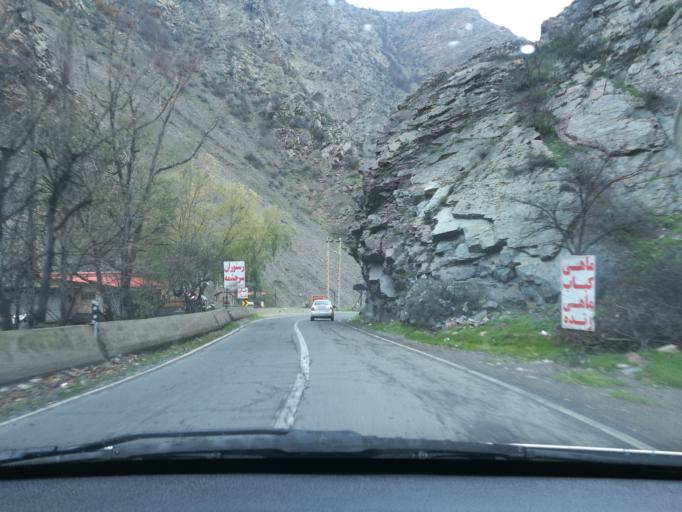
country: IR
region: Mazandaran
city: Chalus
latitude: 36.3016
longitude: 51.2476
